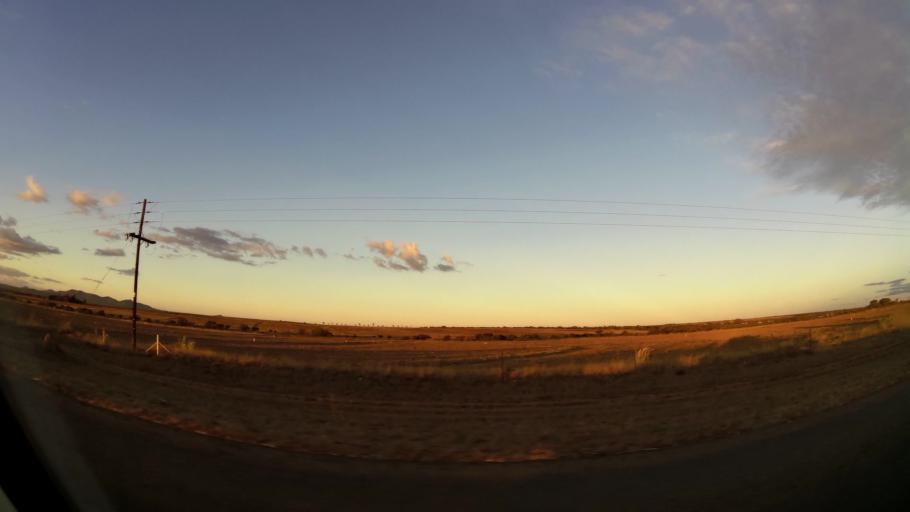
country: ZA
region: Limpopo
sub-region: Capricorn District Municipality
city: Polokwane
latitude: -23.7891
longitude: 29.4761
